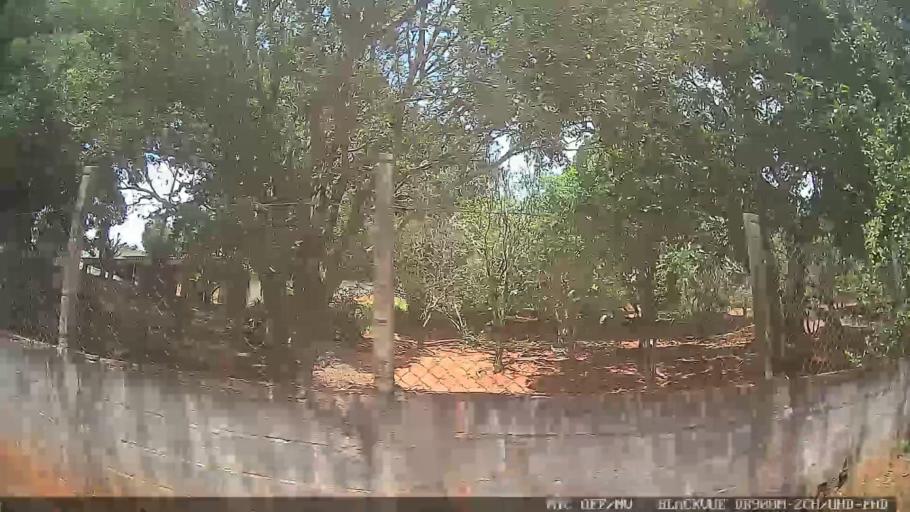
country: BR
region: Sao Paulo
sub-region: Braganca Paulista
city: Braganca Paulista
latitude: -23.0220
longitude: -46.5422
